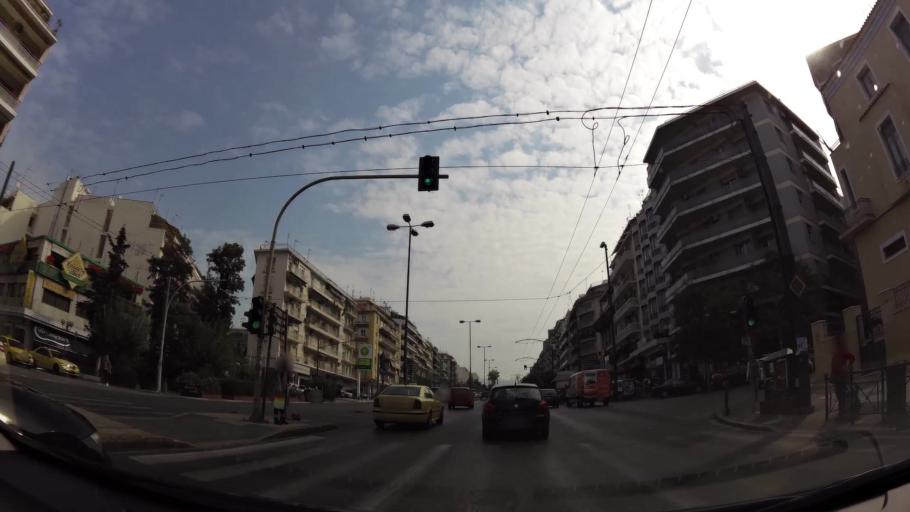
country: GR
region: Attica
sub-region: Nomarchia Athinas
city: Kipseli
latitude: 37.9890
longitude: 23.7477
